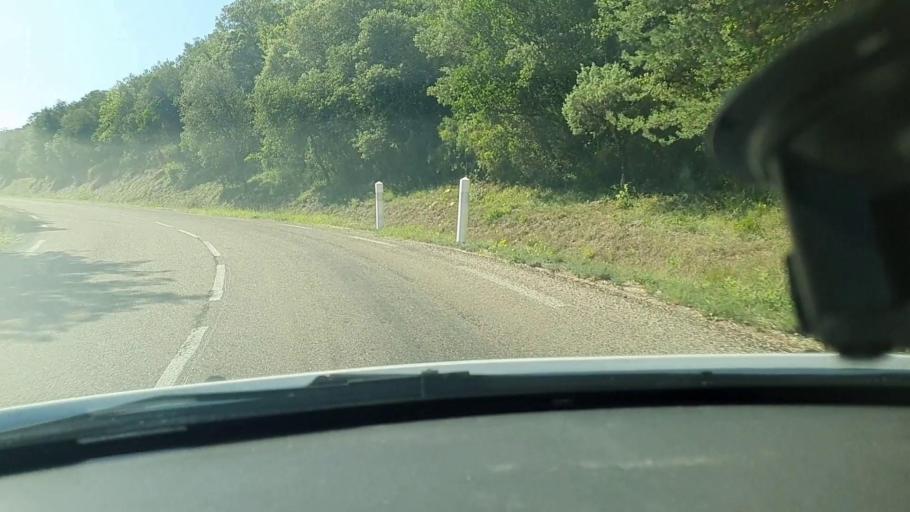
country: FR
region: Languedoc-Roussillon
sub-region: Departement du Gard
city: Saint-Paulet-de-Caisson
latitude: 44.2459
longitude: 4.5758
